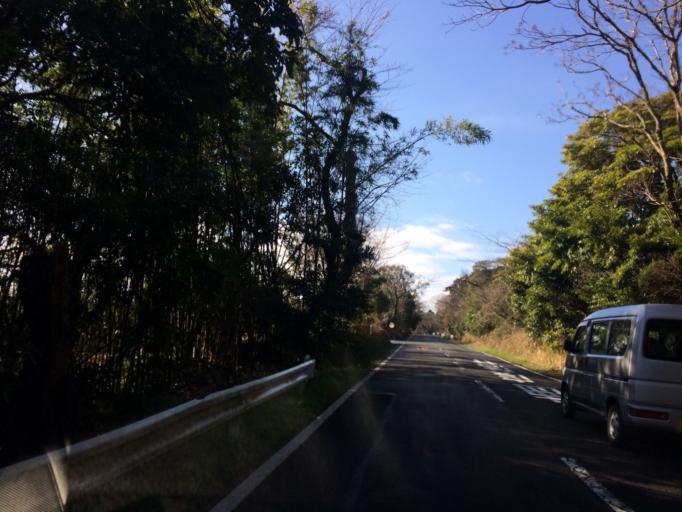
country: JP
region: Shizuoka
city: Shizuoka-shi
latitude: 34.9704
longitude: 138.4483
